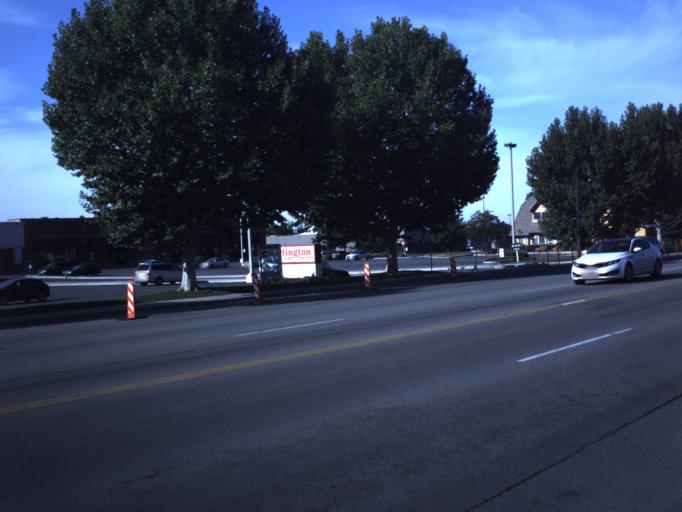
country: US
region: Utah
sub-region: Utah County
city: Orem
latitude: 40.2735
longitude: -111.6869
